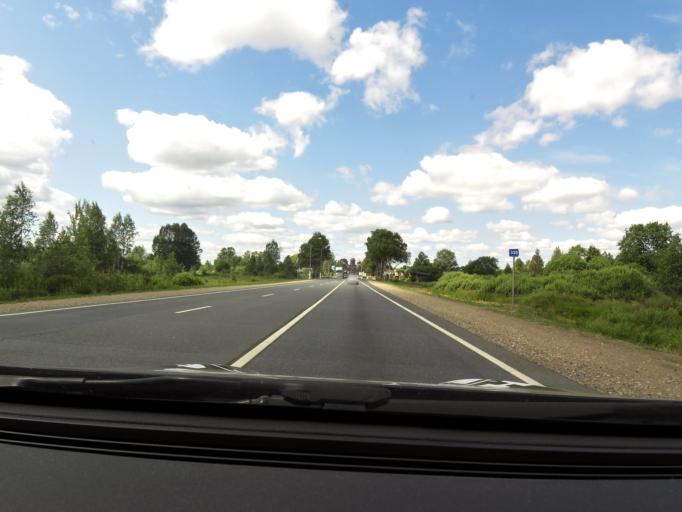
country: RU
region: Tverskaya
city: Kuzhenkino
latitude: 57.7213
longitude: 34.0993
